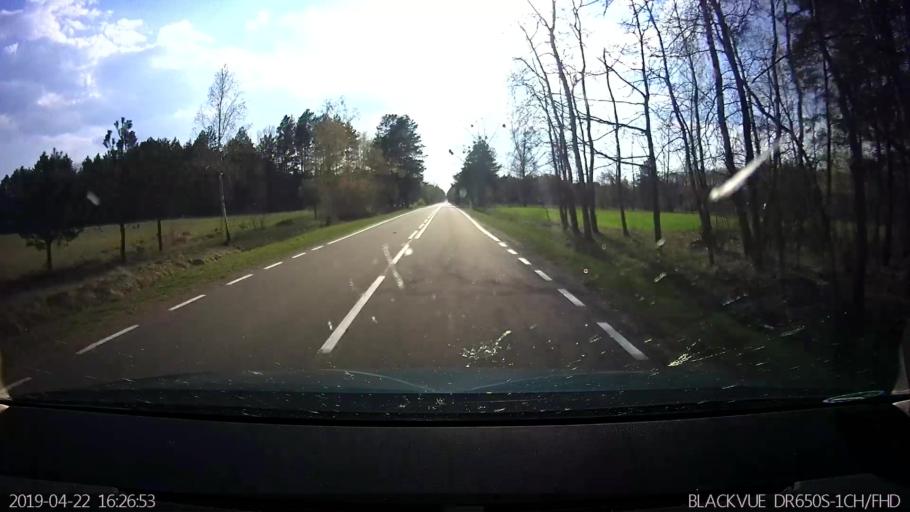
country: PL
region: Podlasie
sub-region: Powiat siemiatycki
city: Milejczyce
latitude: 52.5483
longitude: 23.2141
